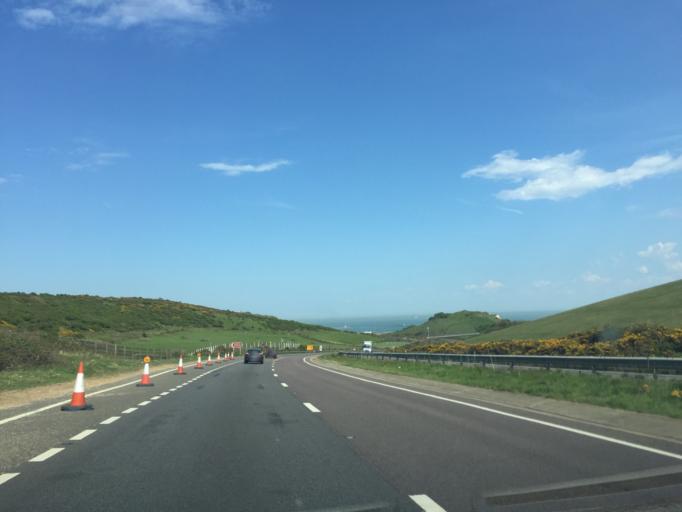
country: GB
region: England
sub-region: Kent
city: Dover
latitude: 51.1095
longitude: 1.2760
